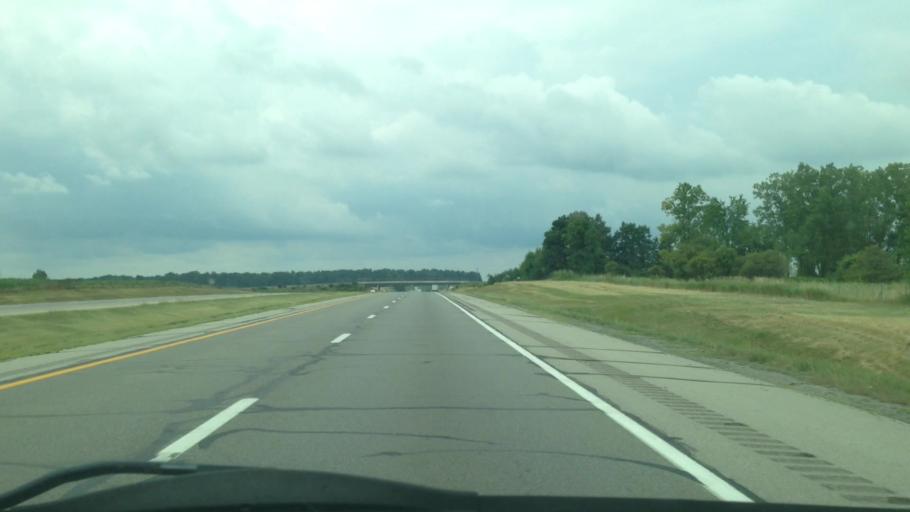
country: US
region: Ohio
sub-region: Williams County
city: Montpelier
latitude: 41.6179
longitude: -84.6671
